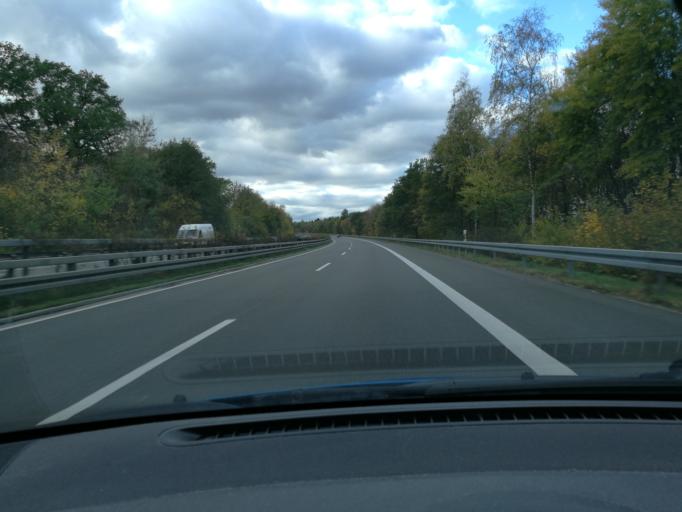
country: DE
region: Lower Saxony
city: Stelle
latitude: 53.3852
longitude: 10.0747
